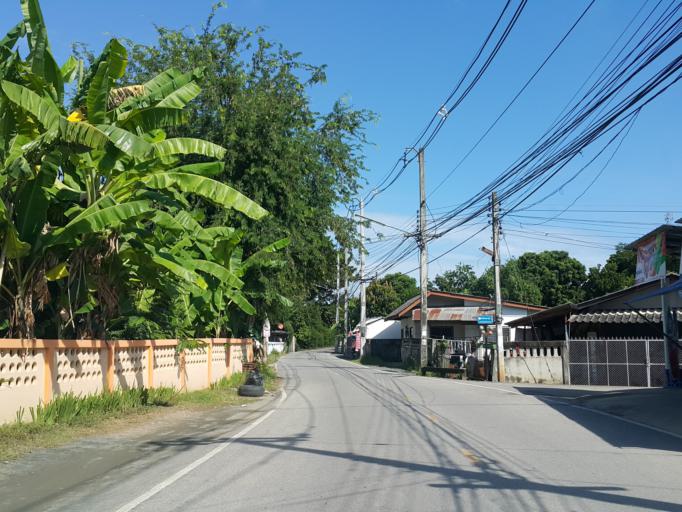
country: TH
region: Chiang Mai
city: San Sai
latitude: 18.8063
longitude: 99.0454
